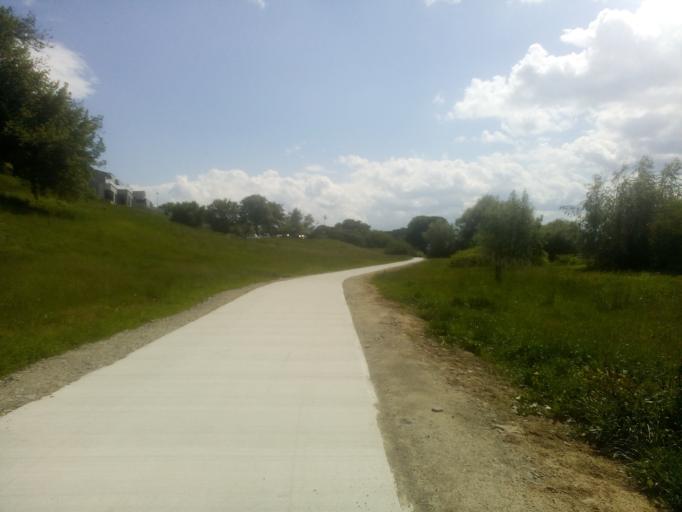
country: PL
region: Lesser Poland Voivodeship
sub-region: Powiat nowosadecki
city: Nowy Sacz
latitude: 49.6281
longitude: 20.6878
